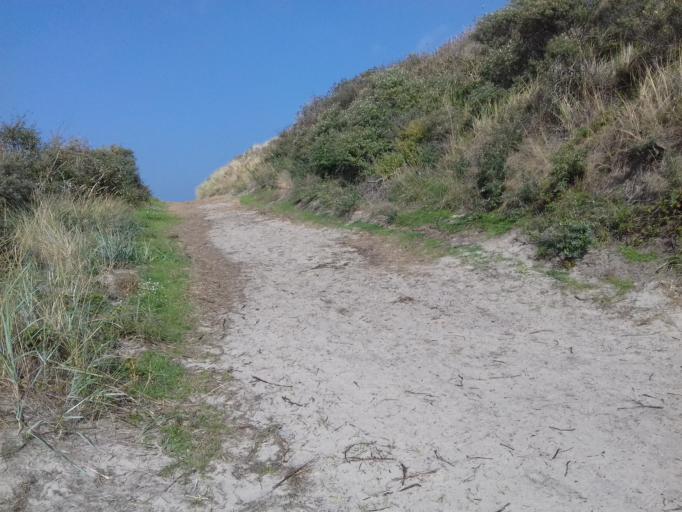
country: DE
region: Lower Saxony
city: Juist
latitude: 53.6817
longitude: 7.0251
